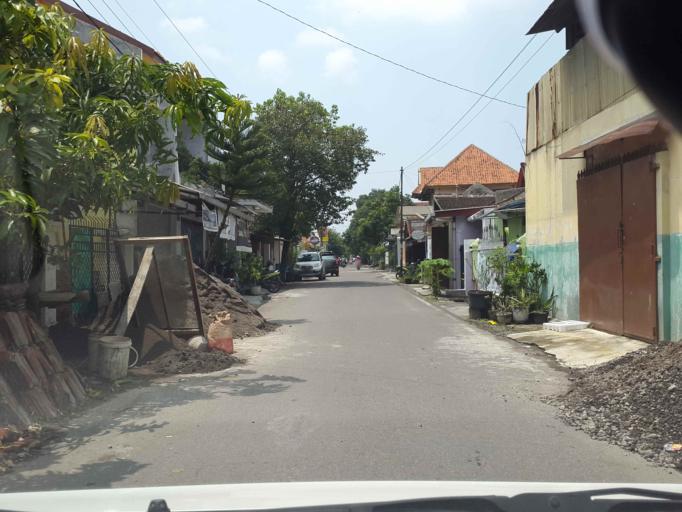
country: ID
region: Central Java
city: Grogol
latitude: -7.5792
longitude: 110.8106
